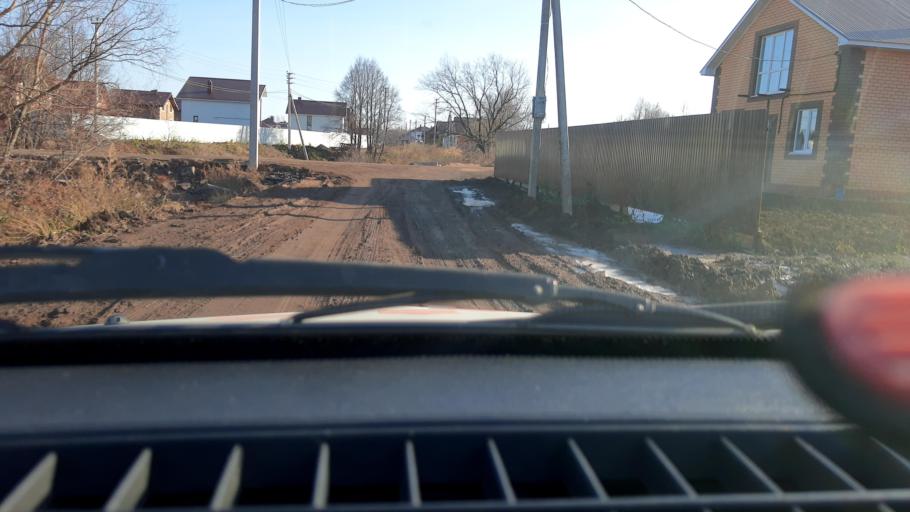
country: RU
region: Bashkortostan
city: Kabakovo
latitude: 54.6263
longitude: 56.1324
